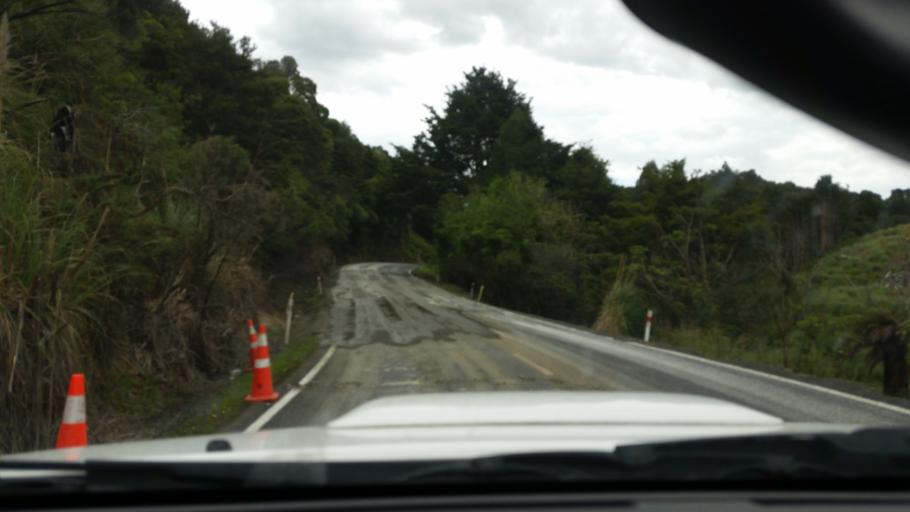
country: NZ
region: Northland
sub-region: Kaipara District
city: Dargaville
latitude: -35.7183
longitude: 173.8584
